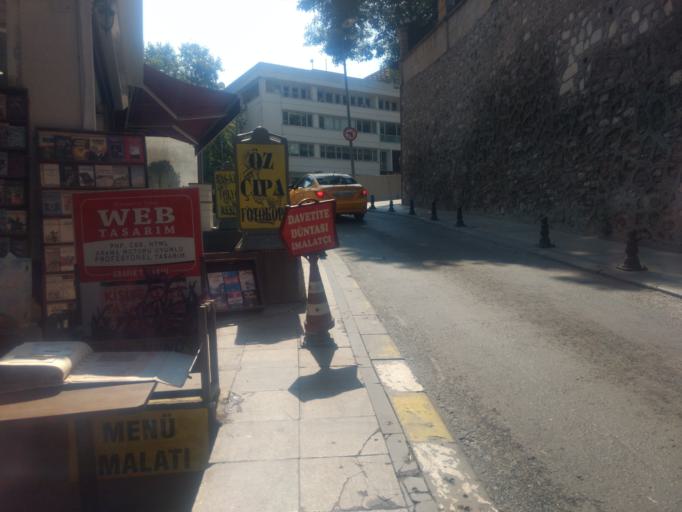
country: TR
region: Istanbul
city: Eminoenue
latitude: 41.0119
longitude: 28.9749
